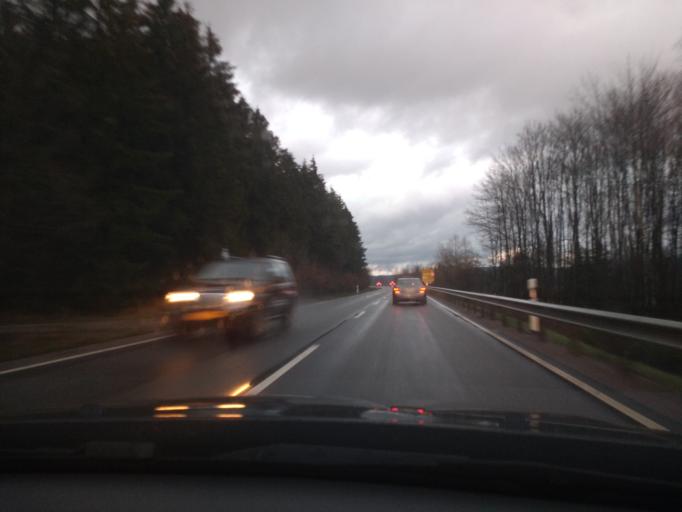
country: DE
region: Rheinland-Pfalz
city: Thalfang
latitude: 49.7621
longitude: 6.9857
